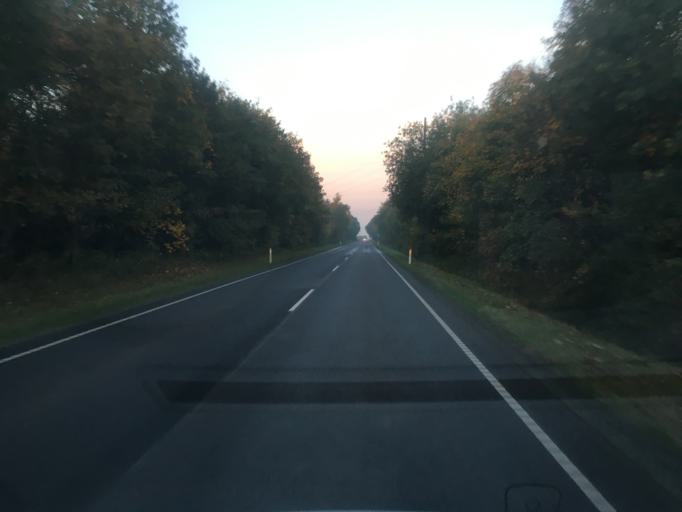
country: DE
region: Schleswig-Holstein
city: Bramstedtlund
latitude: 54.9736
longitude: 9.1227
